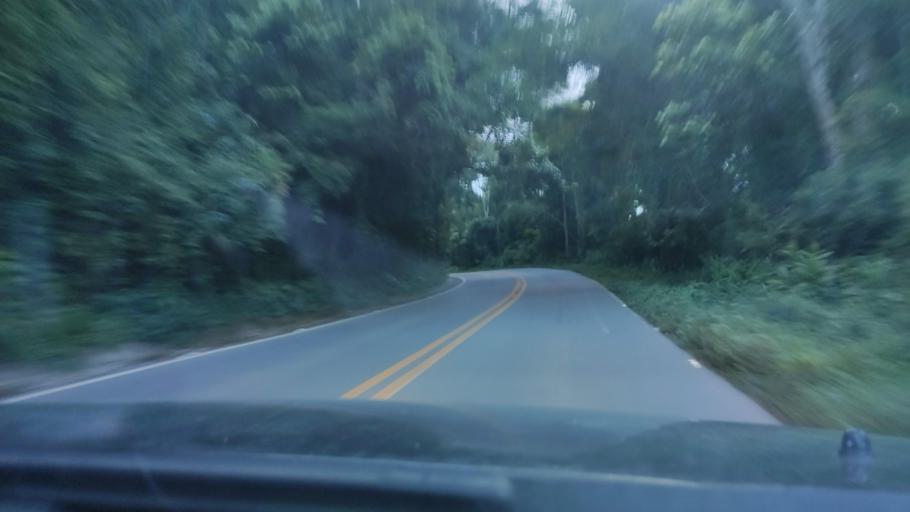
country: BR
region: Sao Paulo
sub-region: Campos Do Jordao
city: Campos do Jordao
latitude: -22.8271
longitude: -45.6810
